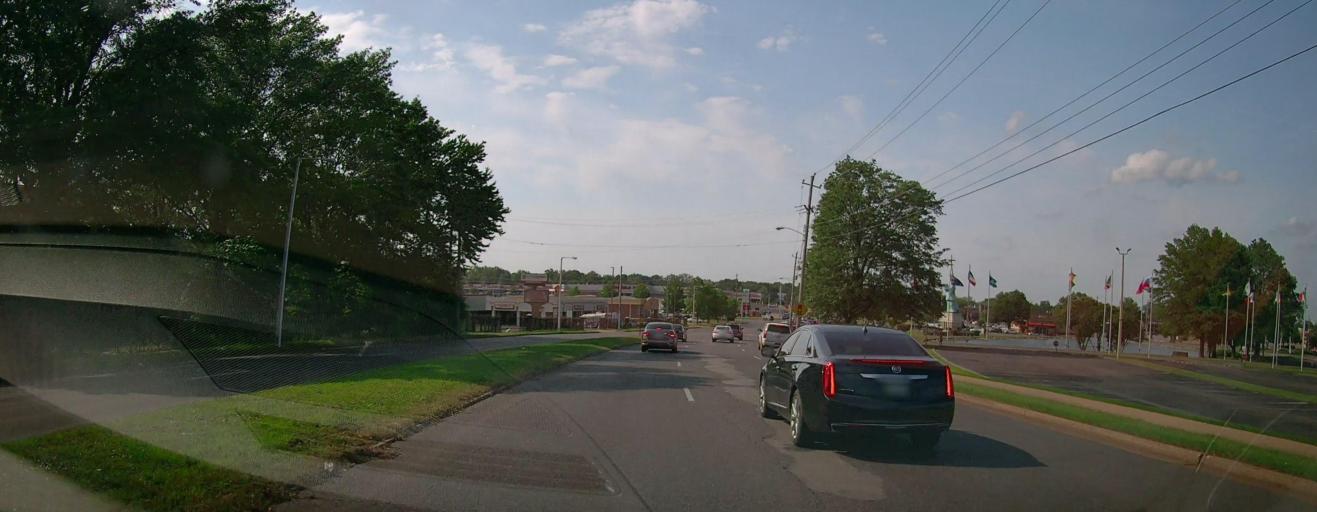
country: US
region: Tennessee
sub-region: Shelby County
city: Germantown
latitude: 35.0471
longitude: -89.8434
